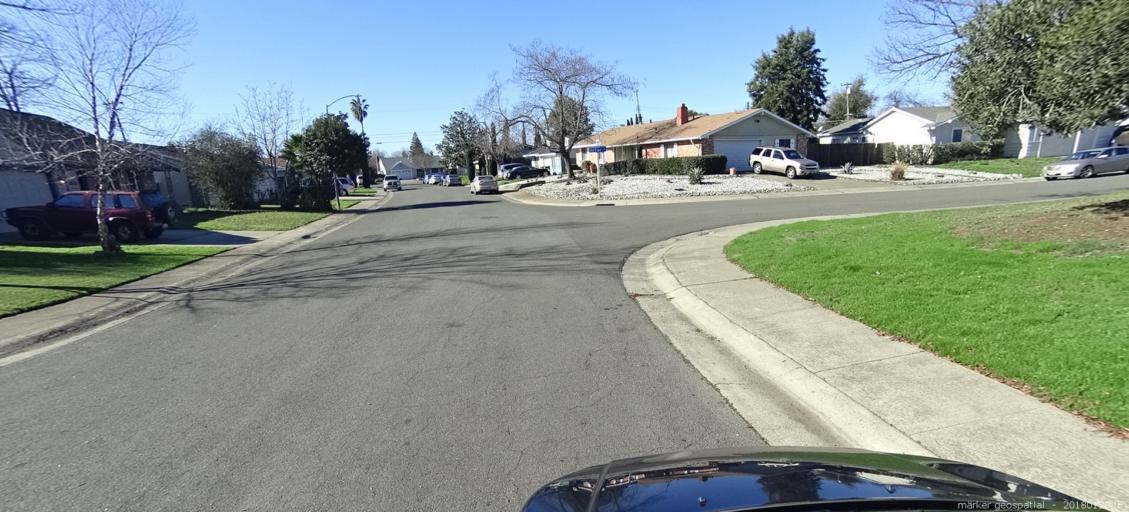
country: US
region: California
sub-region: Sacramento County
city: Rancho Cordova
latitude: 38.5669
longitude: -121.3208
